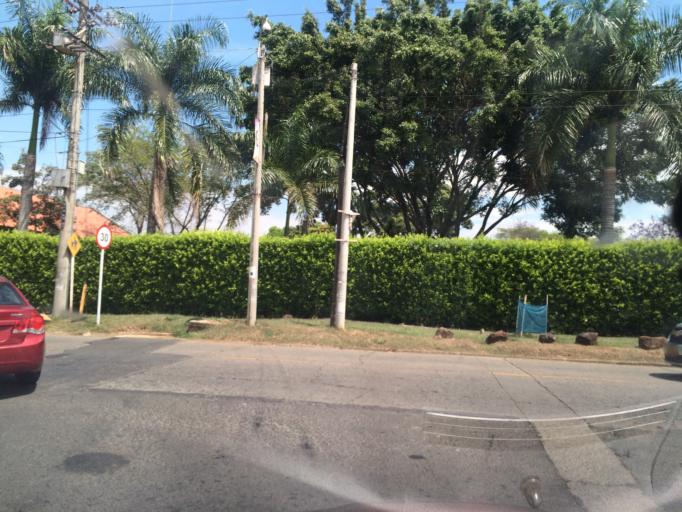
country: CO
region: Valle del Cauca
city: Jamundi
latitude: 3.3425
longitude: -76.5447
